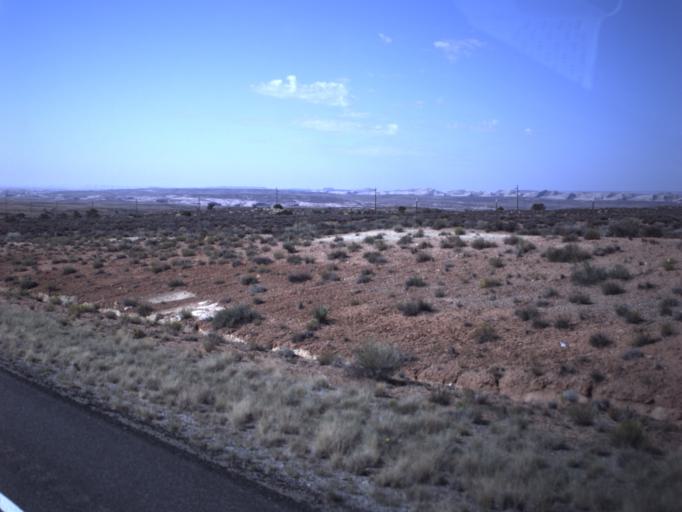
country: US
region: Utah
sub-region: San Juan County
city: Blanding
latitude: 37.3781
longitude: -109.5038
